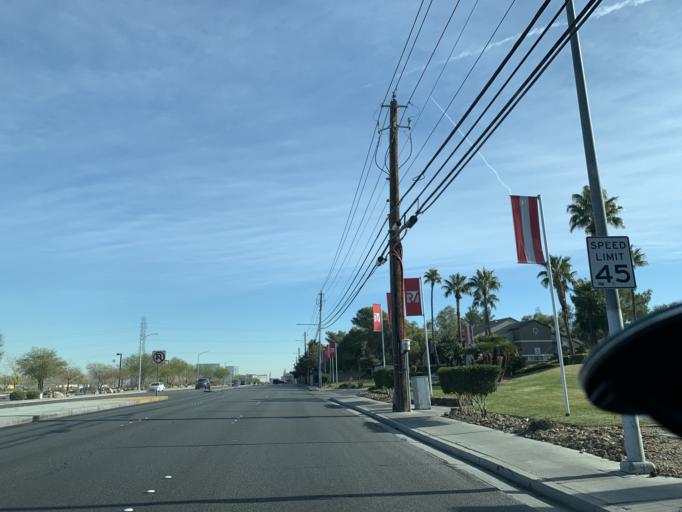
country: US
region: Nevada
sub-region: Clark County
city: Spring Valley
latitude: 36.1003
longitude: -115.2156
